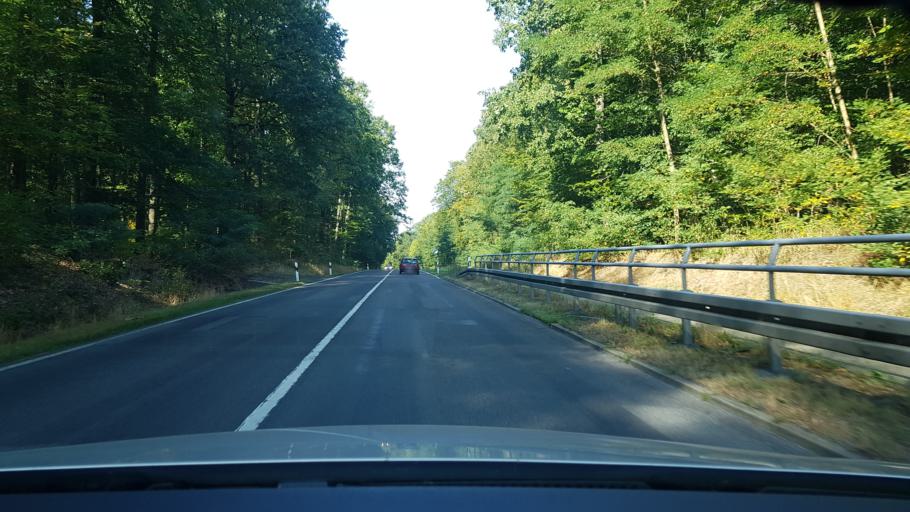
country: DE
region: Brandenburg
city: Mixdorf
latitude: 52.1335
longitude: 14.4474
